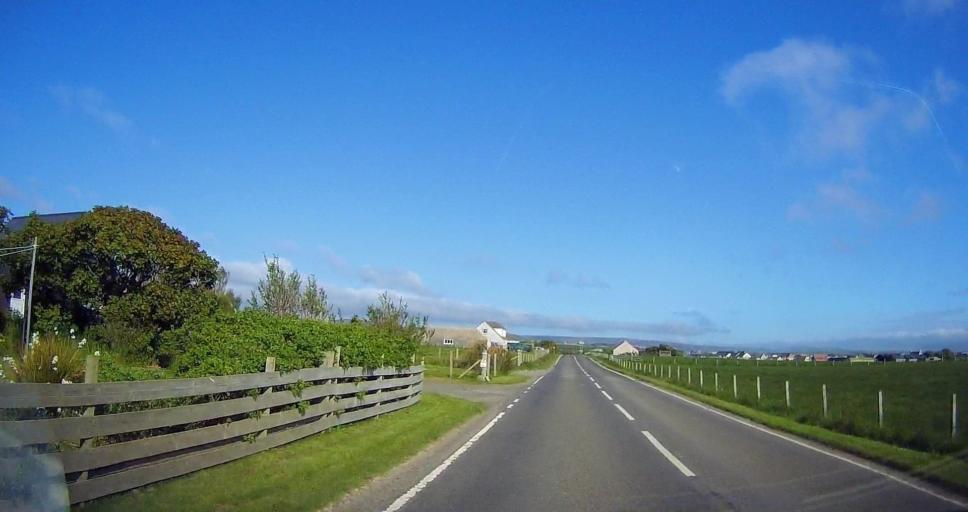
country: GB
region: Scotland
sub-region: Orkney Islands
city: Stromness
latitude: 59.0741
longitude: -3.2446
